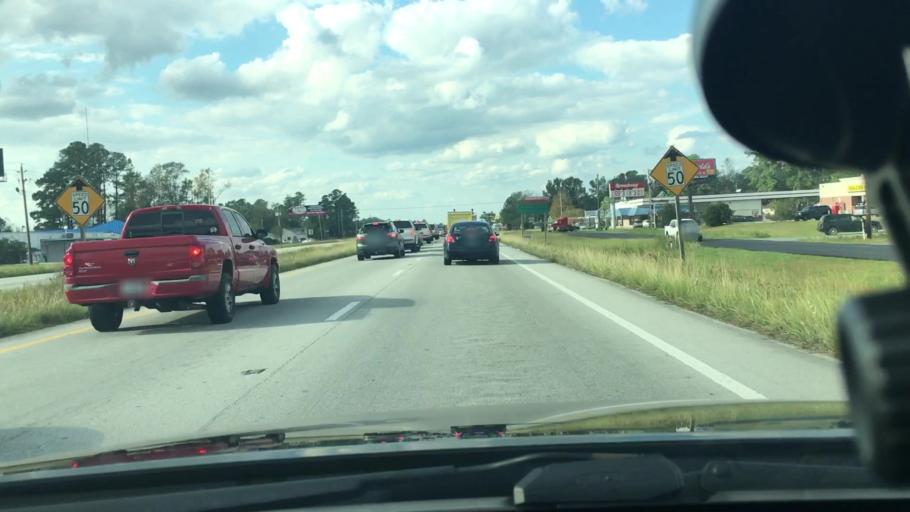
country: US
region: North Carolina
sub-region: Craven County
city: James City
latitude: 35.0633
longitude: -77.0215
